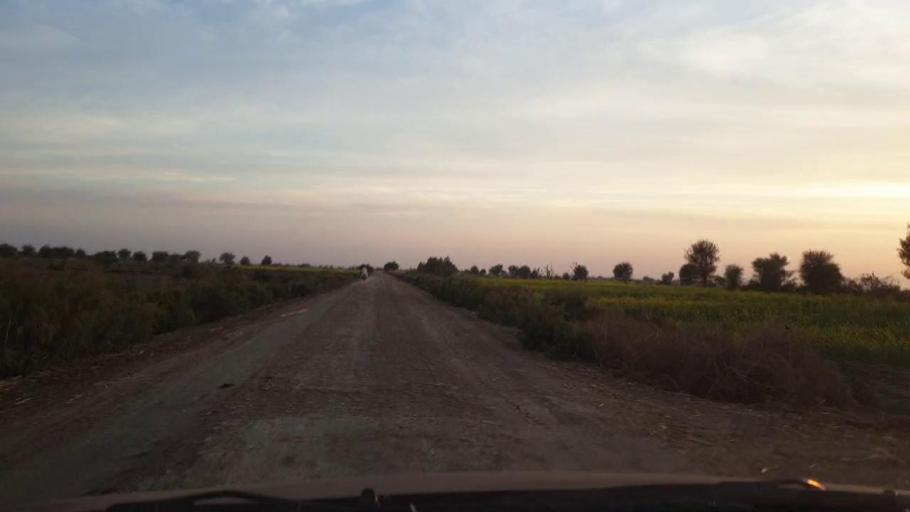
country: PK
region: Sindh
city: Sinjhoro
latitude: 26.0972
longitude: 68.7970
